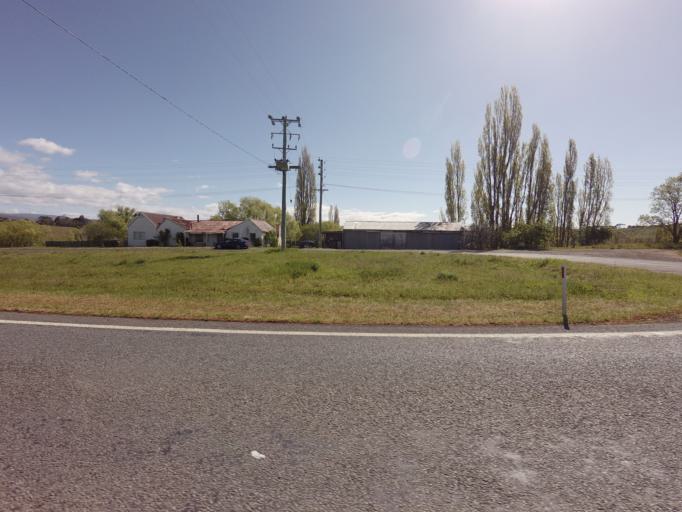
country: AU
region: Tasmania
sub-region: Derwent Valley
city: New Norfolk
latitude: -42.6887
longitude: 146.9419
